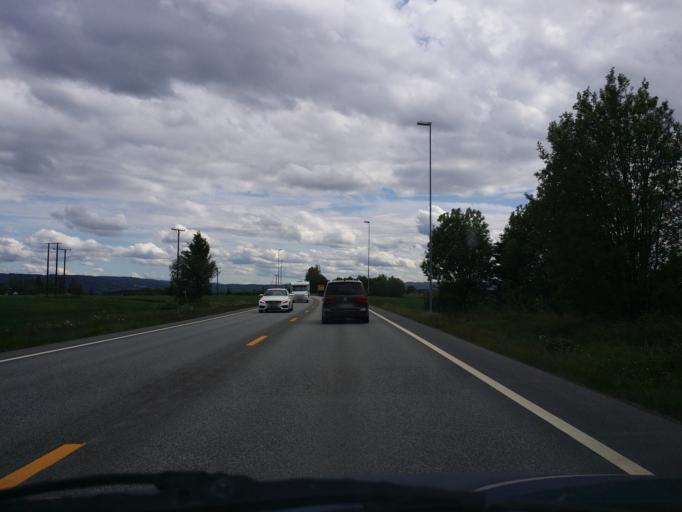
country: NO
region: Hedmark
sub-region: Stange
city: Stange
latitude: 60.7305
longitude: 11.2169
